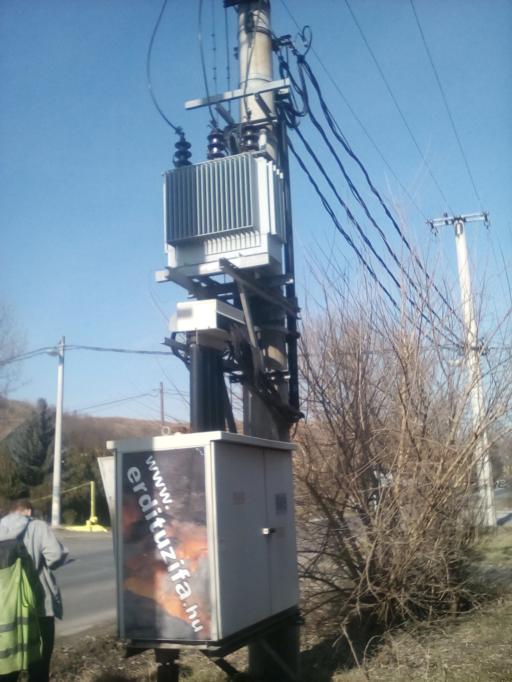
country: HU
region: Pest
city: Soskut
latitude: 47.4085
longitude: 18.8324
